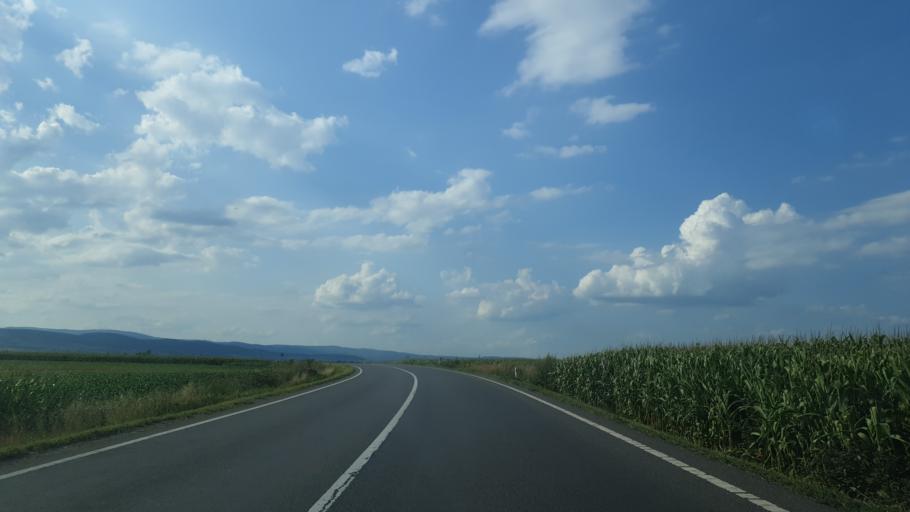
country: RO
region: Covasna
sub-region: Comuna Chichis
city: Chichis
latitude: 45.7913
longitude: 25.8065
